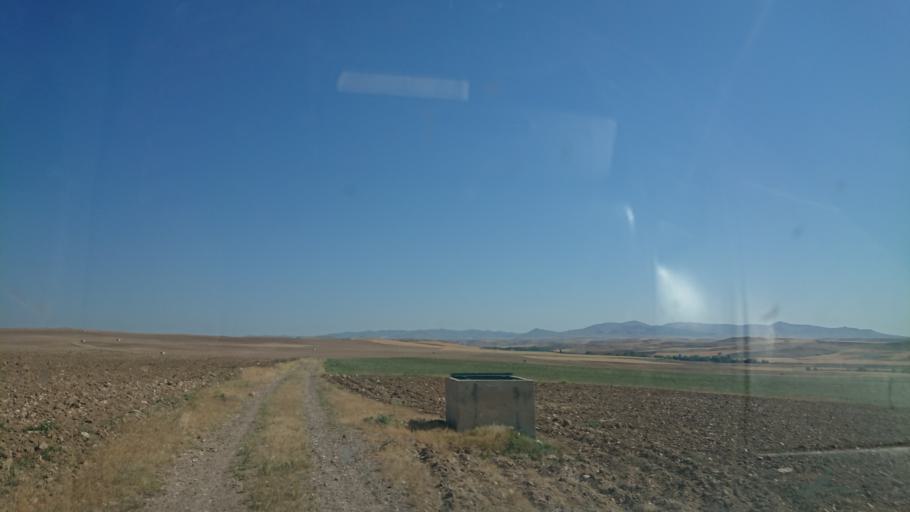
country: TR
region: Aksaray
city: Sariyahsi
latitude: 39.0472
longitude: 33.8903
